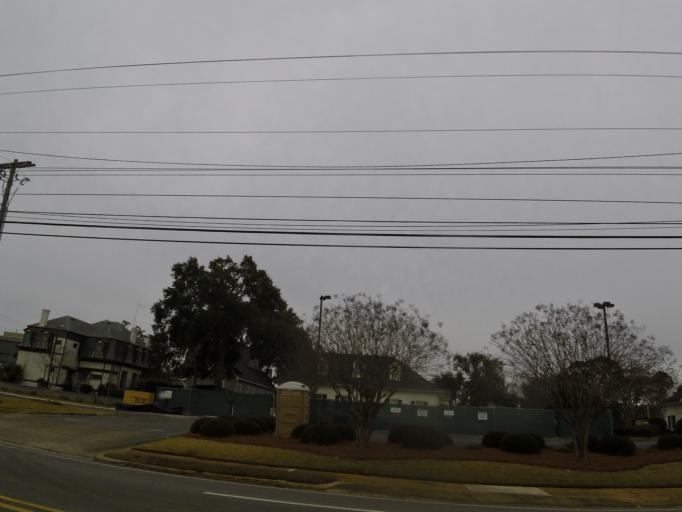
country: US
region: Georgia
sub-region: Thomas County
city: Thomasville
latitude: 30.8395
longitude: -83.9834
